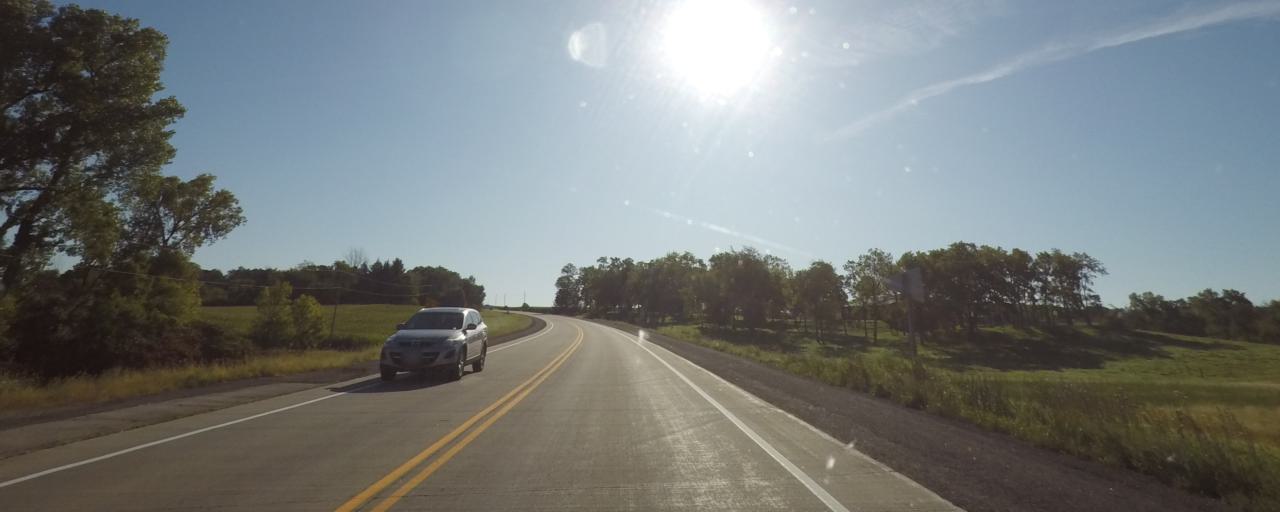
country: US
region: Wisconsin
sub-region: Dane County
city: Cottage Grove
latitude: 43.0288
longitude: -89.1725
